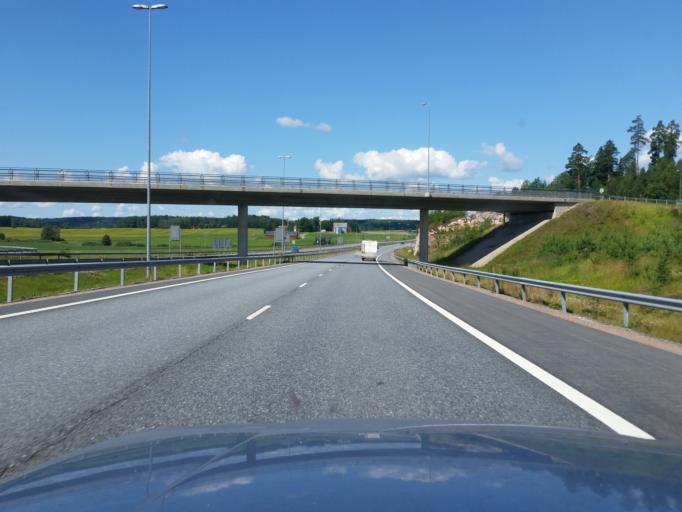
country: FI
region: Varsinais-Suomi
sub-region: Salo
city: Muurla
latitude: 60.3792
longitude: 23.3217
